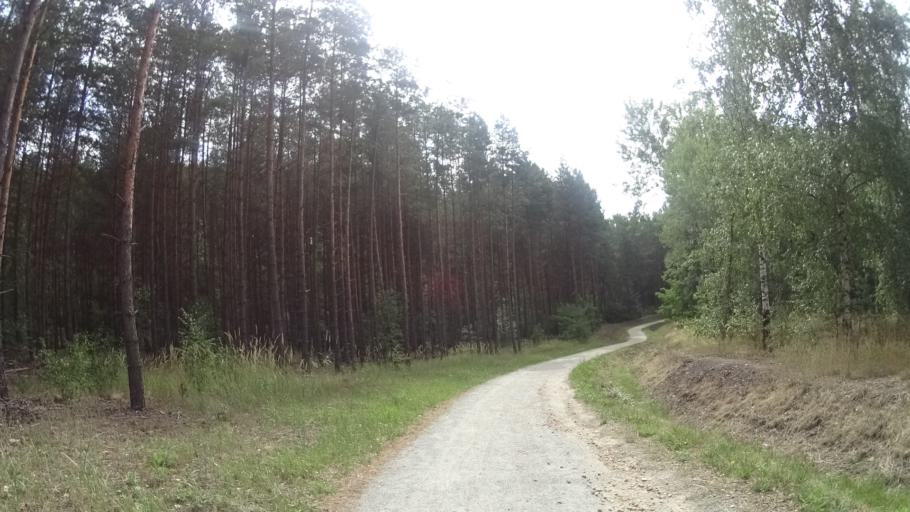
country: PL
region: Lubusz
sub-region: Powiat zarski
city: Leknica
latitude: 51.5408
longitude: 14.7777
